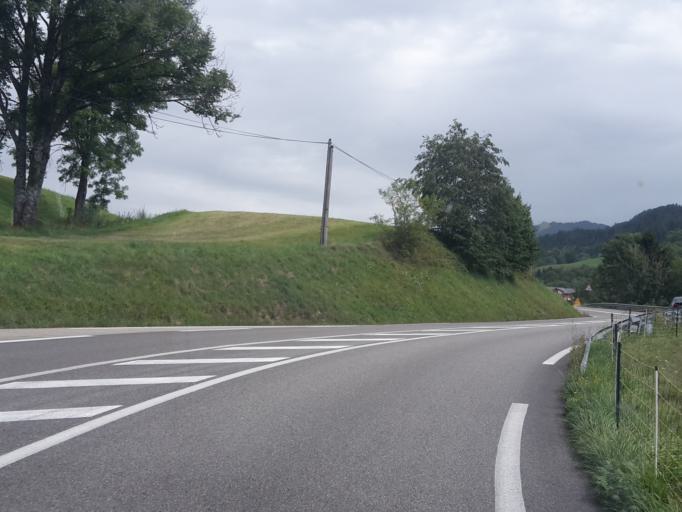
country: FR
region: Rhone-Alpes
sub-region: Departement de la Haute-Savoie
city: Praz-sur-Arly
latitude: 45.8247
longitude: 6.5365
